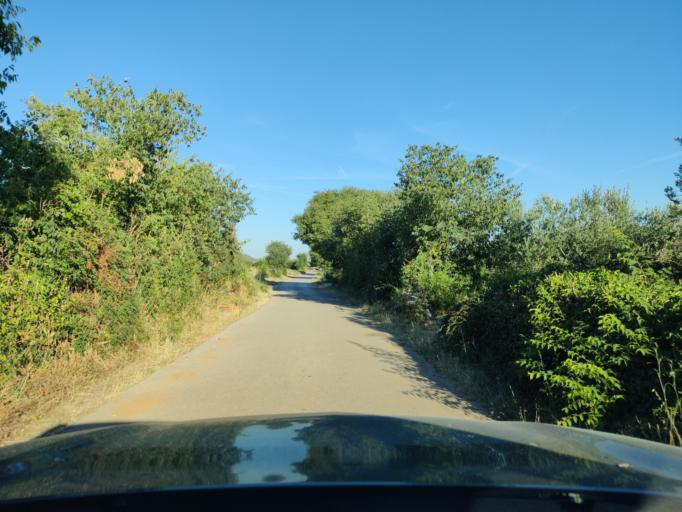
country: HR
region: Sibensko-Kniniska
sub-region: Grad Sibenik
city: Pirovac
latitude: 43.8633
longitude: 15.7001
